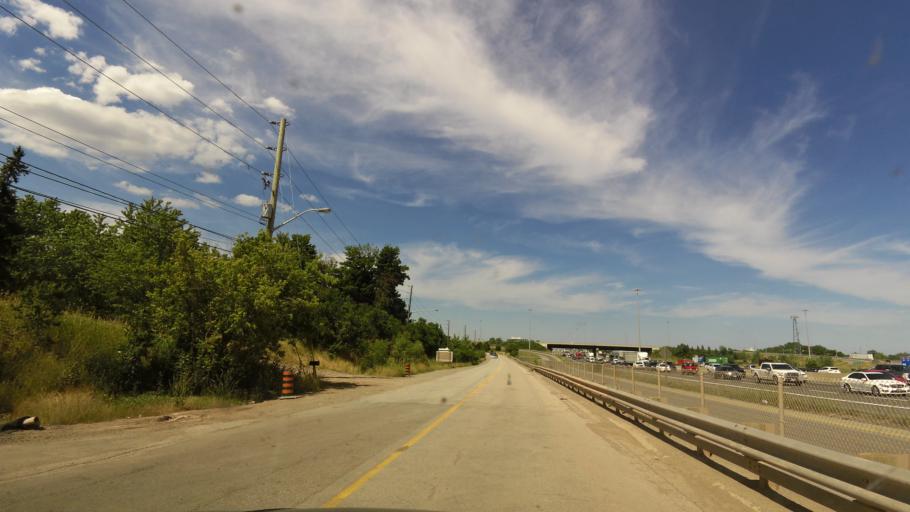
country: CA
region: Ontario
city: Oakville
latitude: 43.4215
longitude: -79.7286
